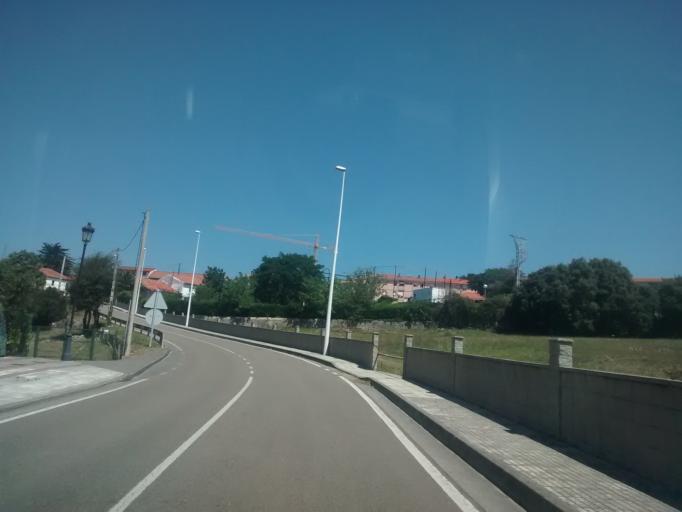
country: ES
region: Cantabria
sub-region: Provincia de Cantabria
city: Arnuero
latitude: 43.4753
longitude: -3.5687
